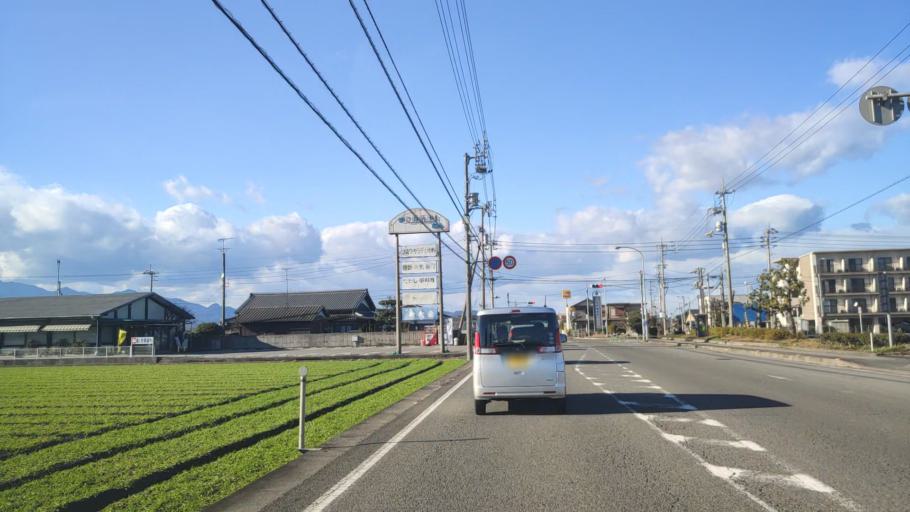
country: JP
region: Ehime
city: Saijo
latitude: 33.9136
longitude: 133.1077
